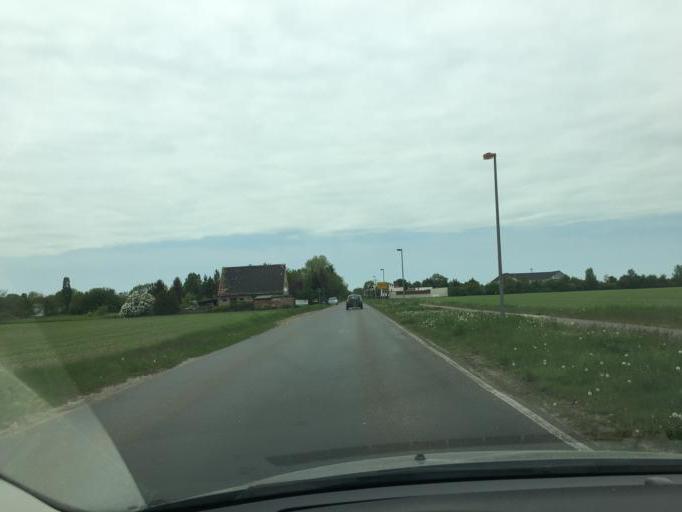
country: DE
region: Saxony
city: Rackwitz
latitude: 51.4017
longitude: 12.4232
